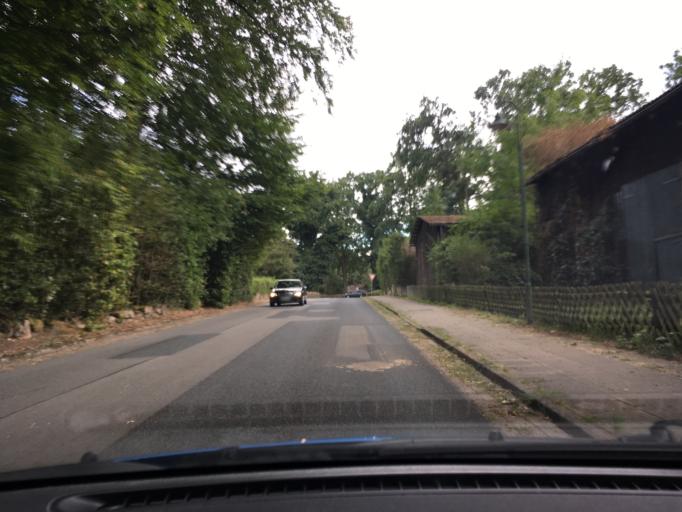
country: DE
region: Lower Saxony
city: Undeloh
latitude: 53.2305
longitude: 9.9176
